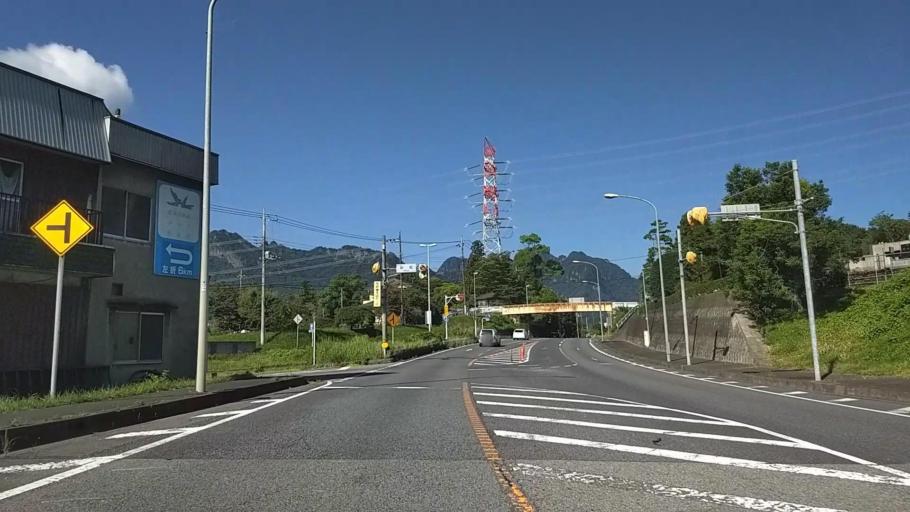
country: JP
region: Gunma
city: Annaka
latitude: 36.3203
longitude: 138.7840
